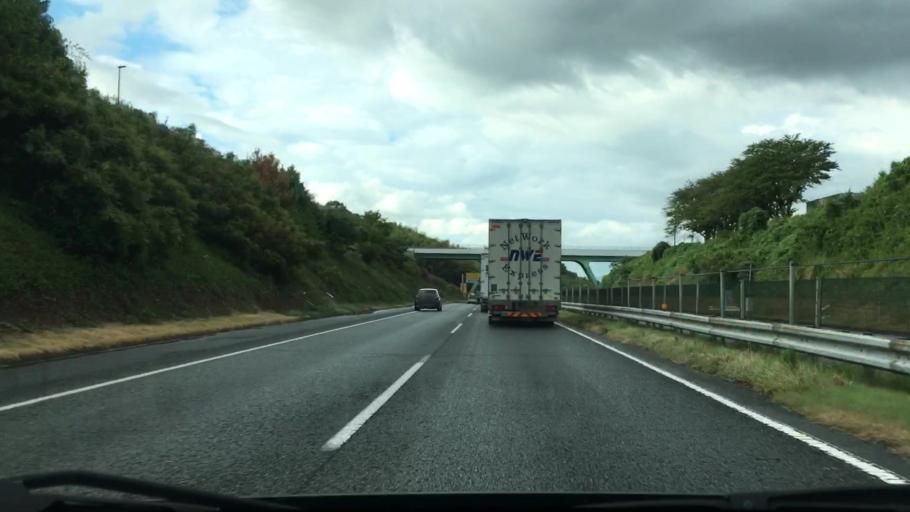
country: JP
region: Fukuoka
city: Koga
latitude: 33.7381
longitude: 130.5187
